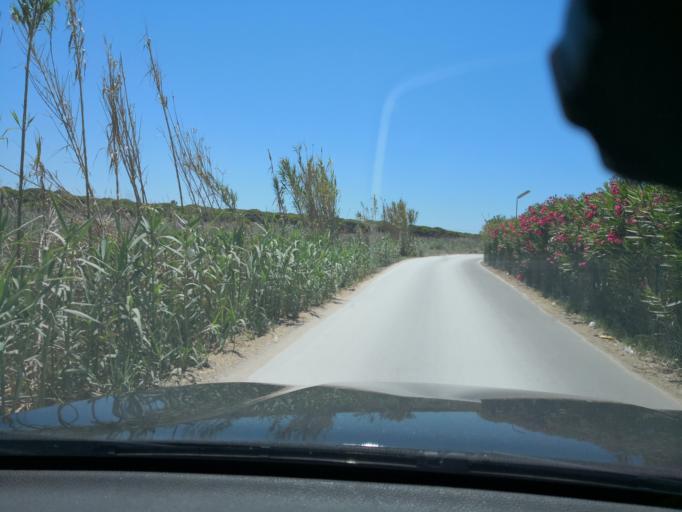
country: PT
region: Faro
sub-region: Loule
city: Quarteira
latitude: 37.0649
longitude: -8.0835
